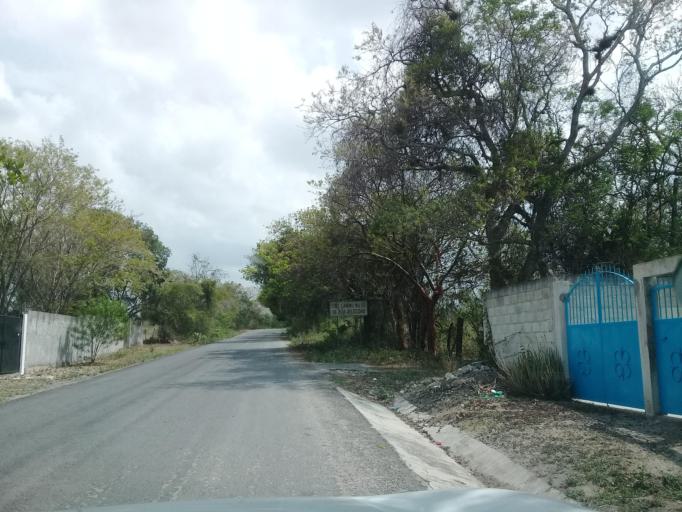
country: MX
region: Veracruz
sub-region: Emiliano Zapata
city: Plan del Rio
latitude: 19.3571
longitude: -96.6613
